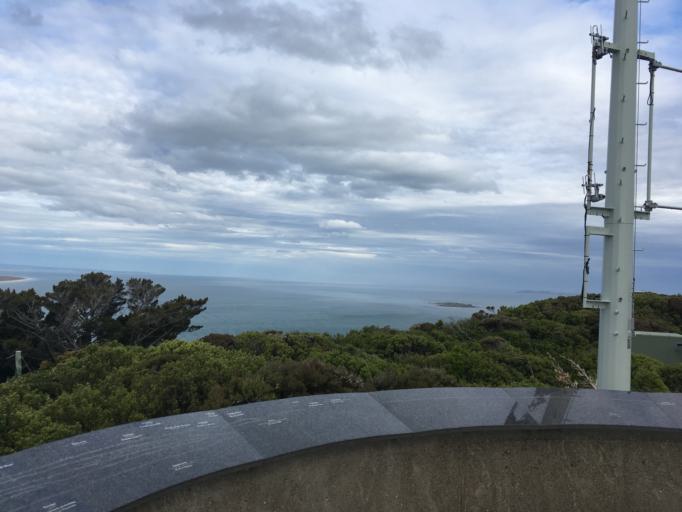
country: NZ
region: Southland
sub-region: Invercargill City
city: Bluff
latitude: -46.6149
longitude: 168.3387
